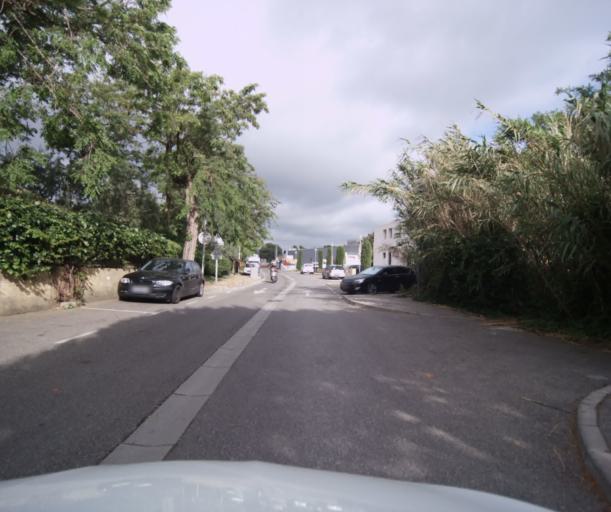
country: FR
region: Provence-Alpes-Cote d'Azur
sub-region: Departement du Var
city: Sanary-sur-Mer
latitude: 43.1230
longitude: 5.8247
